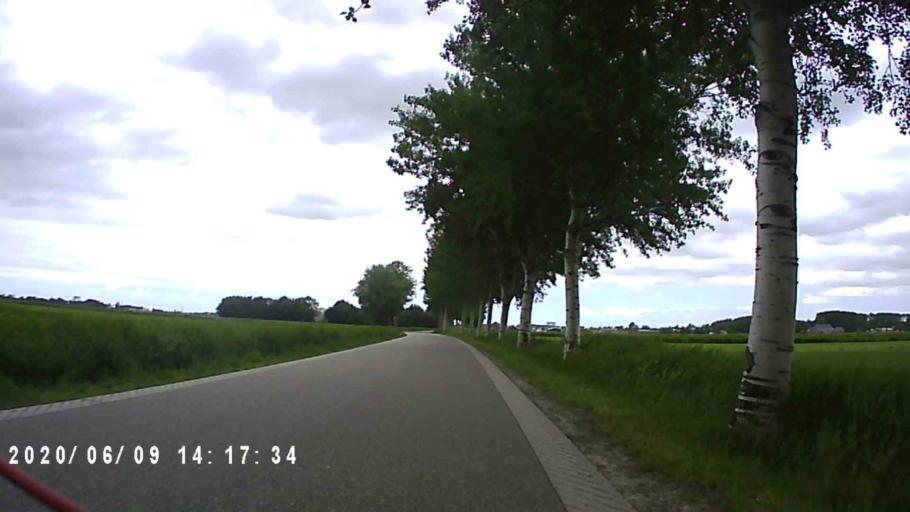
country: NL
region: Groningen
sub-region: Gemeente Bedum
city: Bedum
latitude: 53.2840
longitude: 6.5927
